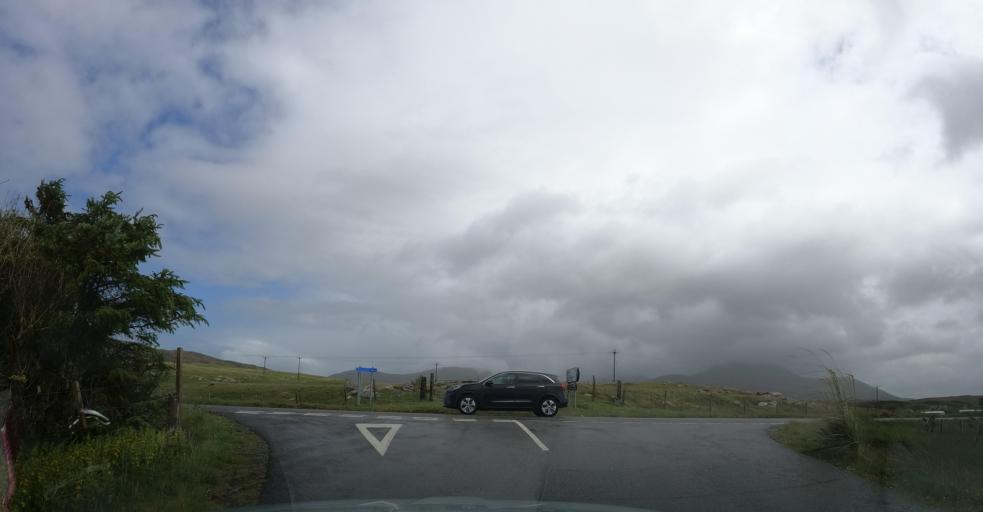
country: GB
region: Scotland
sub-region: Eilean Siar
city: Isle of South Uist
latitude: 57.2907
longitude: -7.3681
